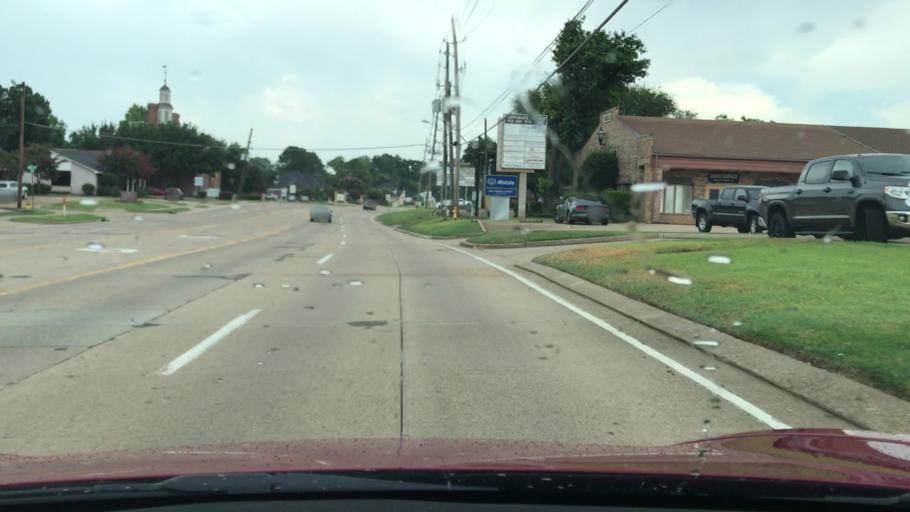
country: US
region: Louisiana
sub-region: Bossier Parish
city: Bossier City
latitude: 32.4439
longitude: -93.7088
